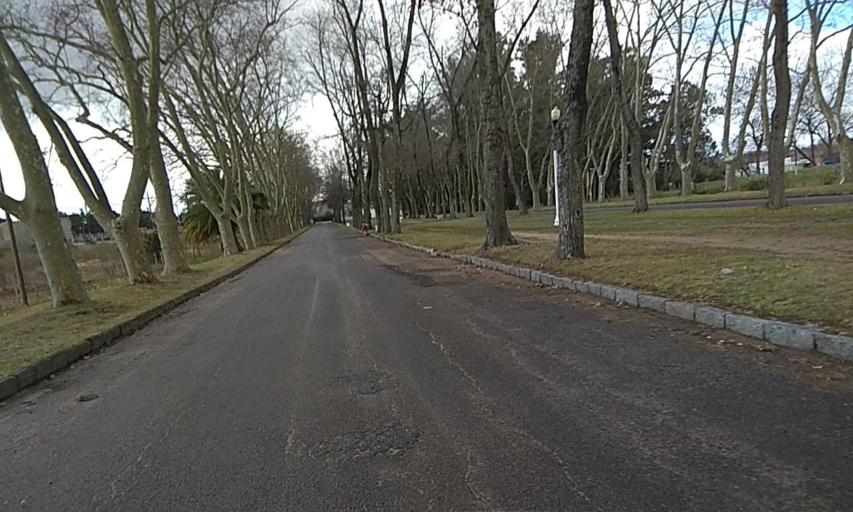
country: UY
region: Florida
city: Florida
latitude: -34.1068
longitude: -56.2267
